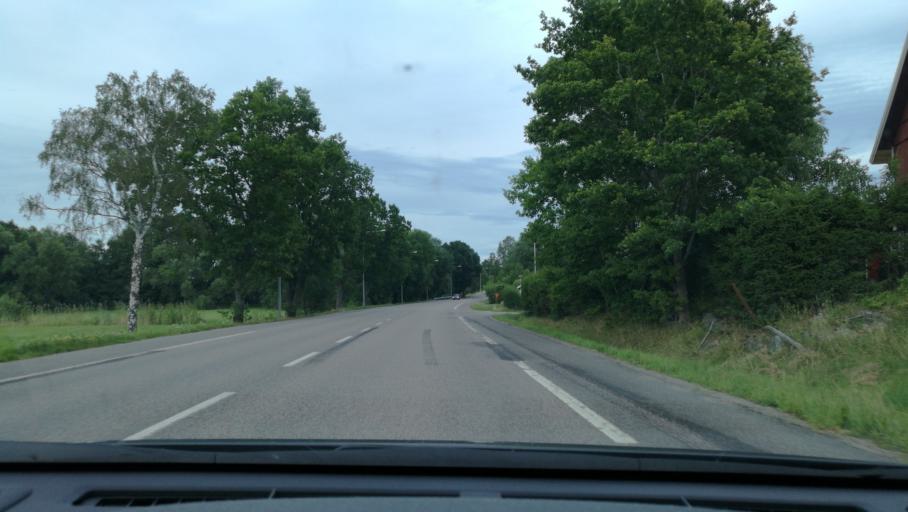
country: SE
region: Vaestmanland
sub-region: Kungsors Kommun
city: Kungsoer
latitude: 59.4224
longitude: 16.0772
